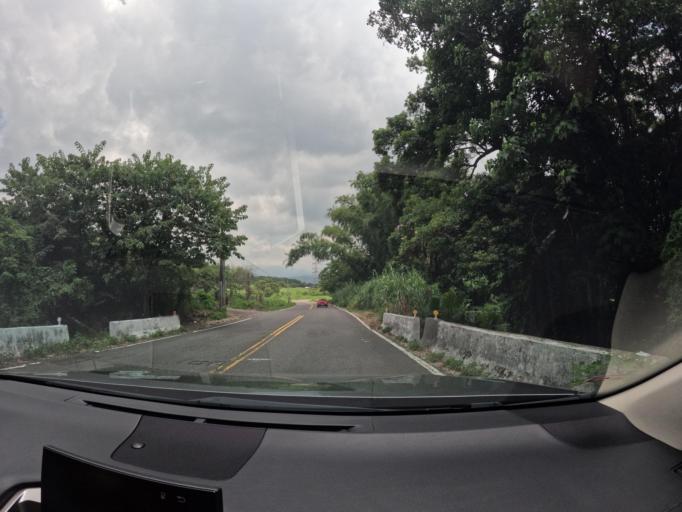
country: TW
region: Taiwan
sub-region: Nantou
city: Nantou
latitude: 23.8860
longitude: 120.6316
